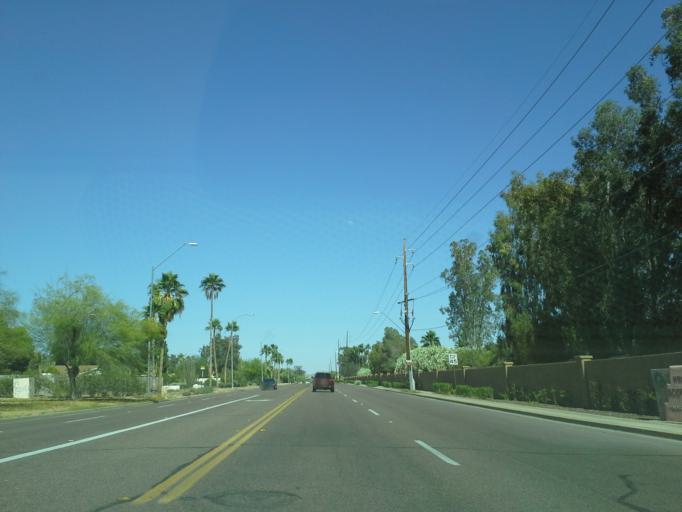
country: US
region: Arizona
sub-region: Maricopa County
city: Paradise Valley
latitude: 33.5970
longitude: -111.9520
